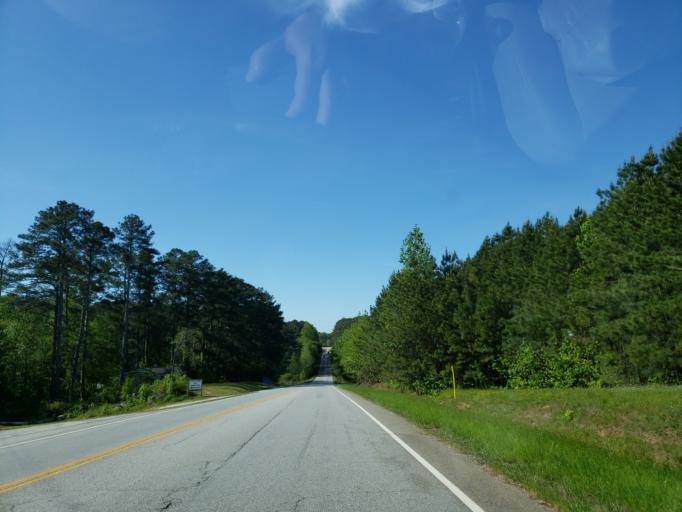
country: US
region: Georgia
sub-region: Haralson County
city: Tallapoosa
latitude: 33.7254
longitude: -85.2810
